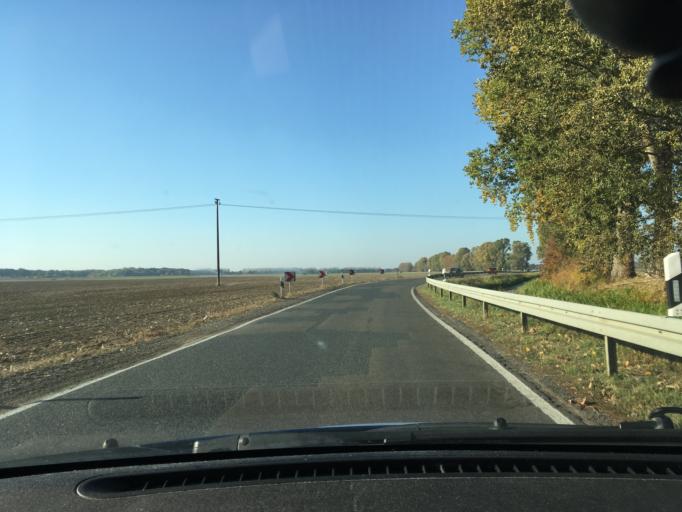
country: DE
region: Mecklenburg-Vorpommern
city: Domitz
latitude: 53.1469
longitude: 11.2607
